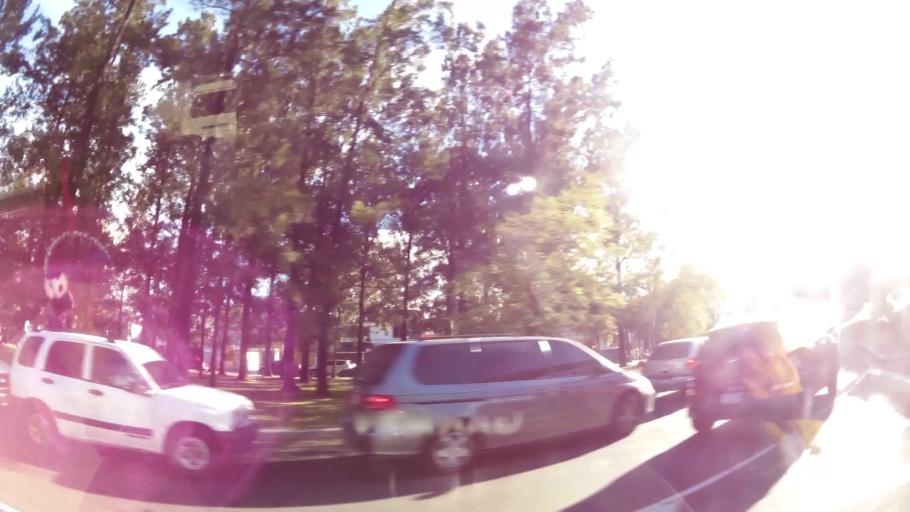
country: GT
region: Guatemala
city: Santa Catarina Pinula
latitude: 14.6038
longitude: -90.5010
